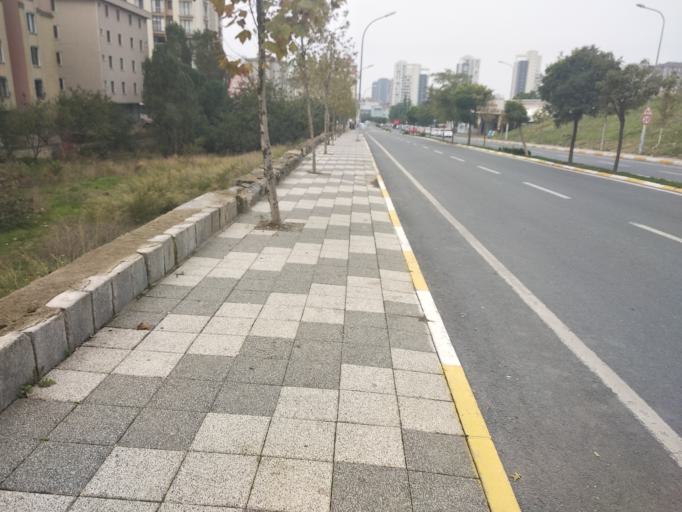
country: TR
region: Istanbul
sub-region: Atasehir
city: Atasehir
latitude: 40.9825
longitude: 29.1275
